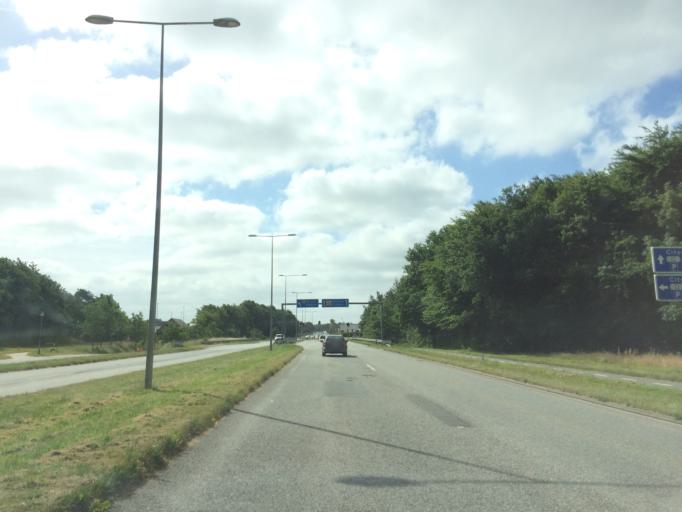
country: DK
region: Central Jutland
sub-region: Herning Kommune
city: Herning
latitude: 56.1439
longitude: 8.9407
